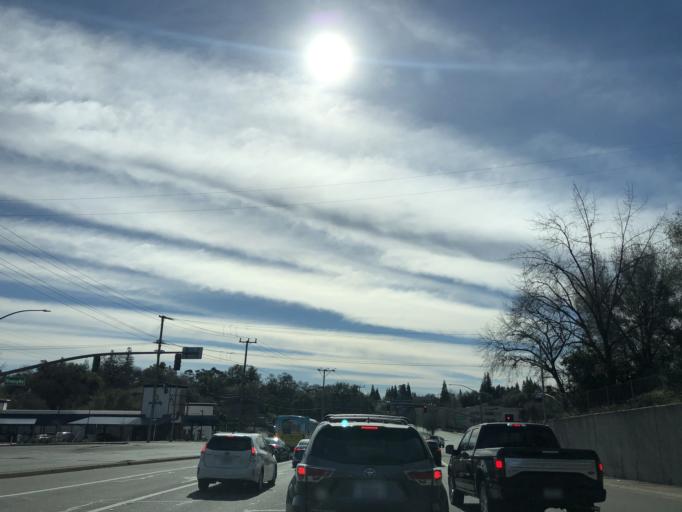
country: US
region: California
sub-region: Sacramento County
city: Fair Oaks
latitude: 38.6454
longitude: -121.2721
